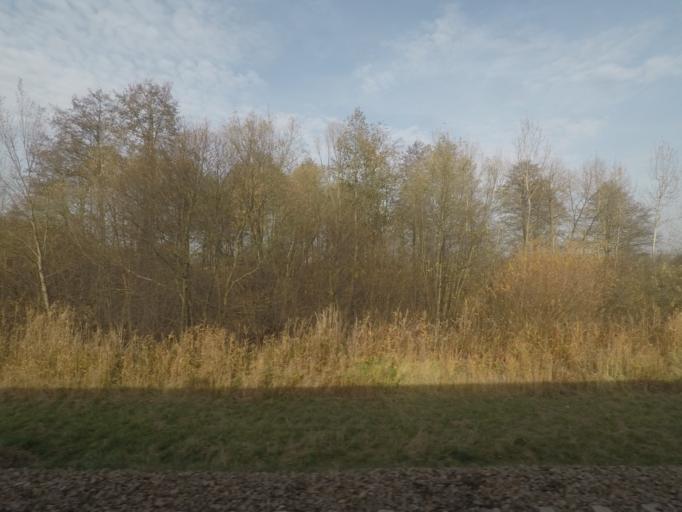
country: PL
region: Subcarpathian Voivodeship
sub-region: Powiat lancucki
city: Gluchow
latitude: 50.0835
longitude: 22.2927
